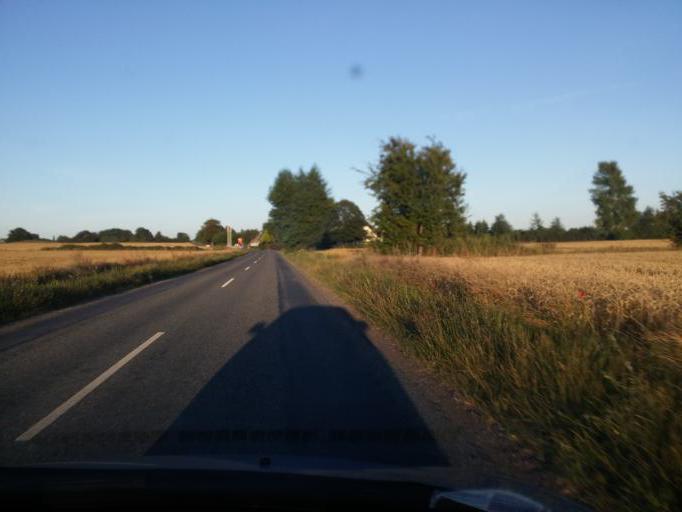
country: DK
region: South Denmark
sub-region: Odense Kommune
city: Bullerup
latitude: 55.3968
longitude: 10.4833
